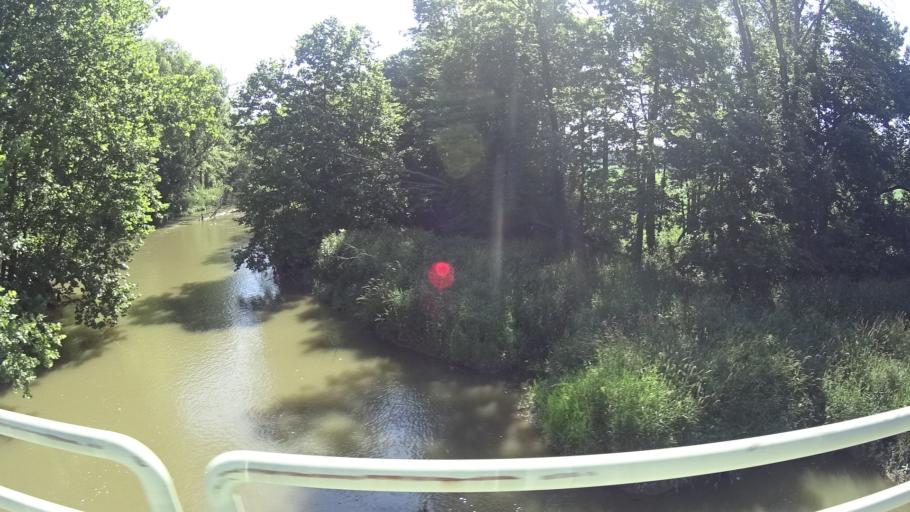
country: US
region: Indiana
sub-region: Madison County
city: Ingalls
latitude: 39.9642
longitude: -85.8150
